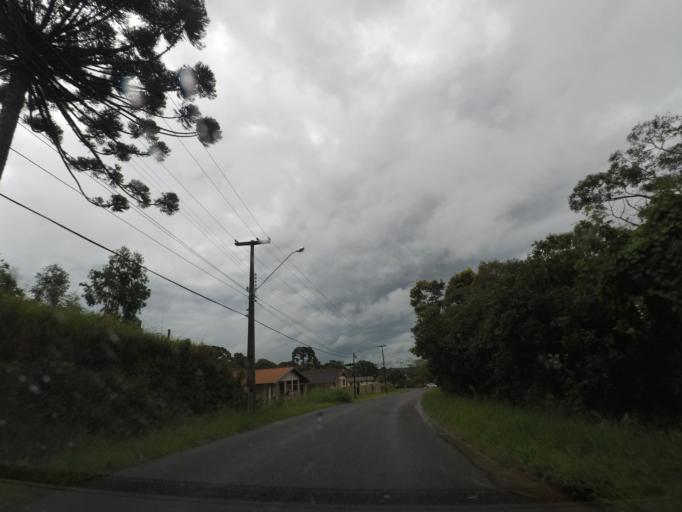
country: BR
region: Parana
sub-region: Campo Largo
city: Campo Largo
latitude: -25.4511
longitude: -49.4545
